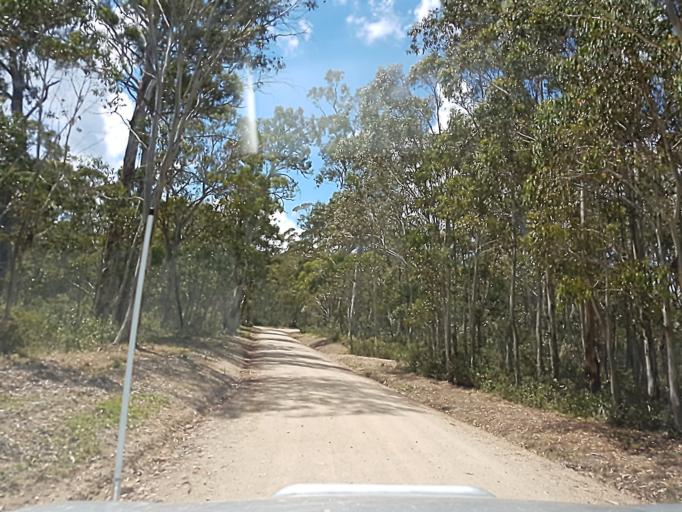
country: AU
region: New South Wales
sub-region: Snowy River
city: Jindabyne
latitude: -36.9042
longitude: 148.1047
